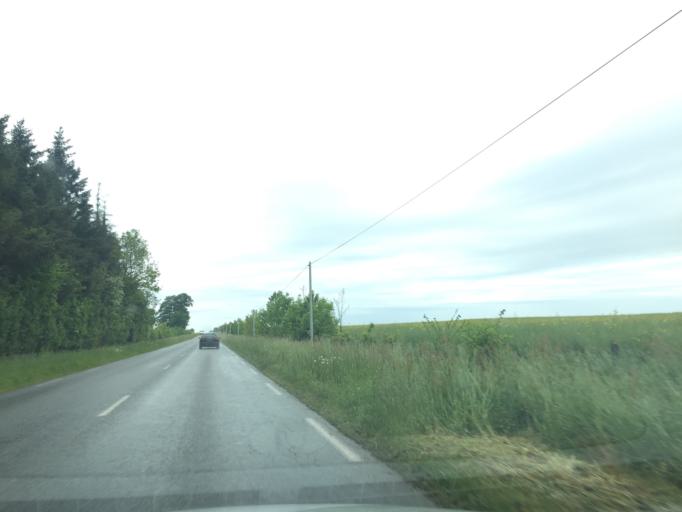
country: FR
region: Brittany
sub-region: Departement des Cotes-d'Armor
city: Crehen
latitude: 48.5534
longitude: -2.1933
